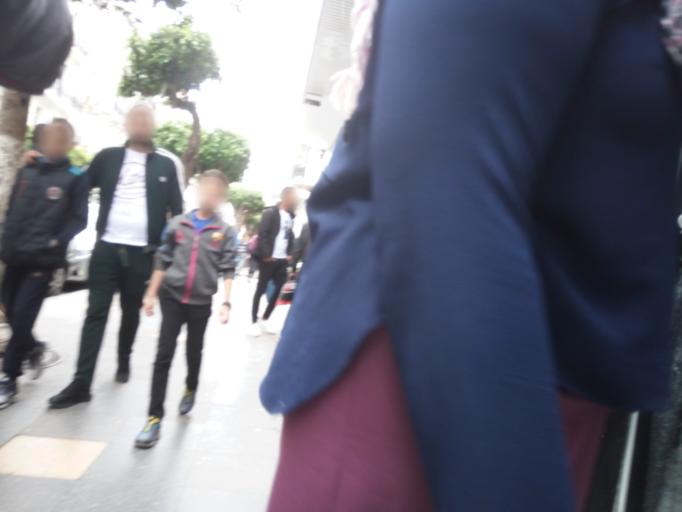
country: DZ
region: Alger
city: Algiers
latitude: 36.7743
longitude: 3.0588
